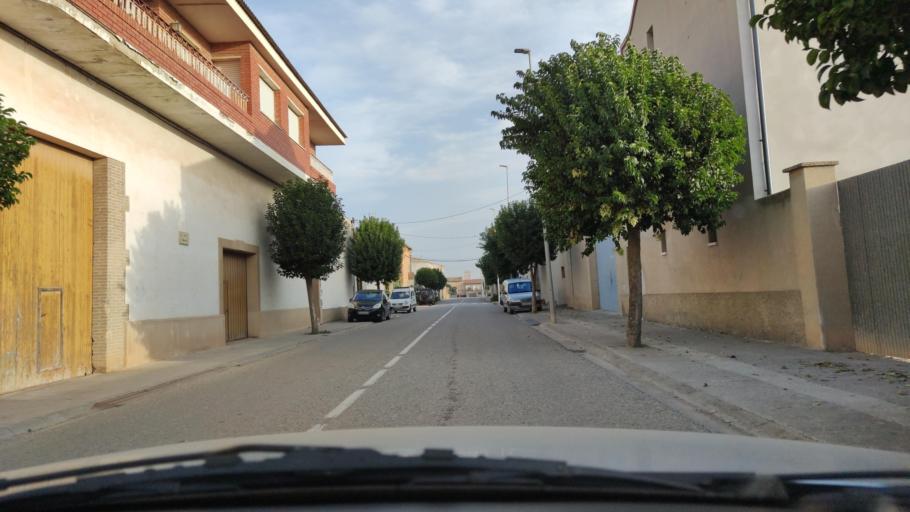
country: ES
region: Catalonia
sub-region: Provincia de Lleida
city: Anglesola
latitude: 41.6532
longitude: 1.0813
